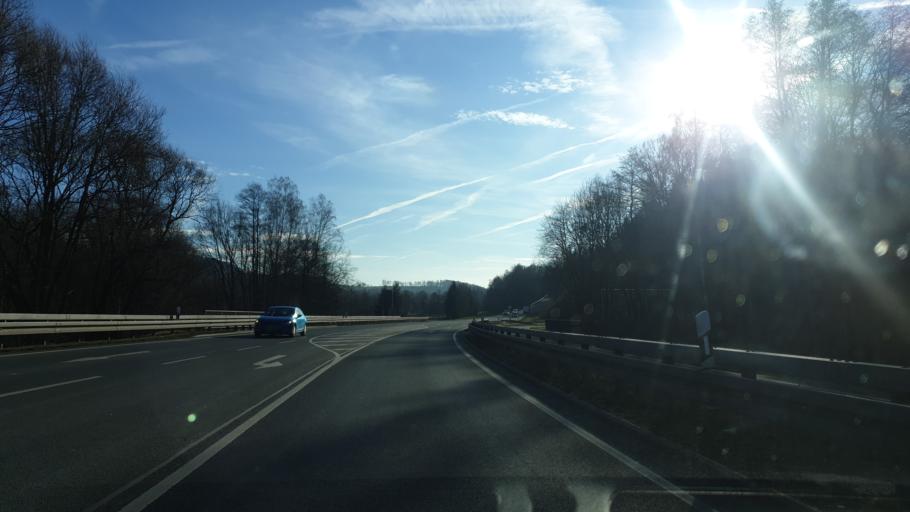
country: DE
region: Saxony
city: Adorf
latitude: 50.3415
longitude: 12.2462
